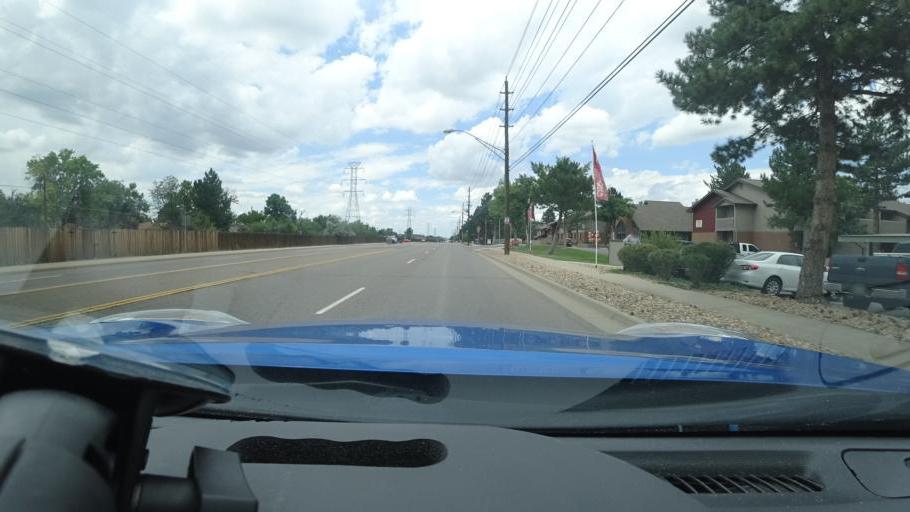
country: US
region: Colorado
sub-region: Adams County
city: Aurora
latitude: 39.7204
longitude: -104.8282
